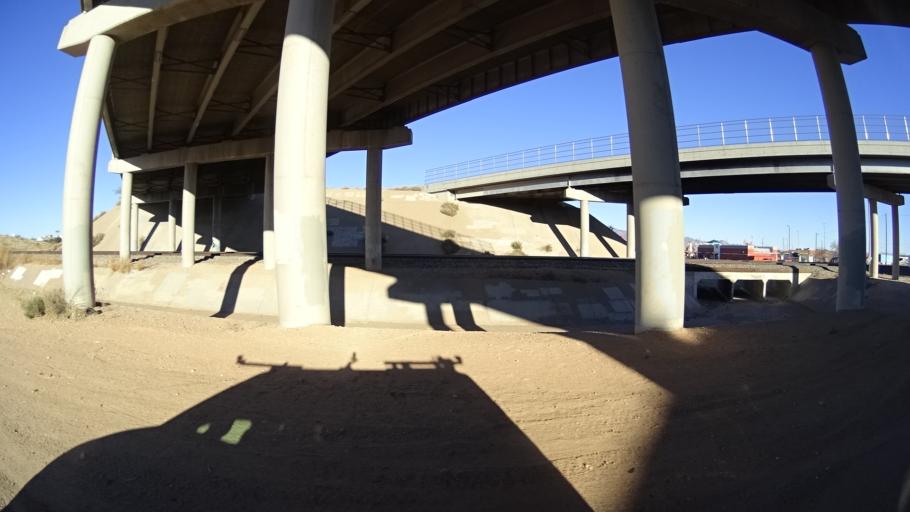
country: US
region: Arizona
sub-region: Mohave County
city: Kingman
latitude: 35.2166
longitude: -114.0069
